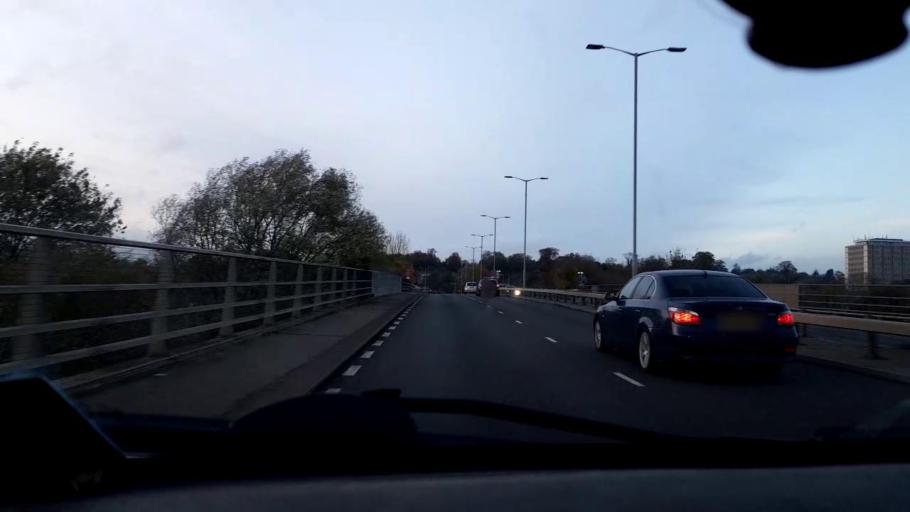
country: GB
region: England
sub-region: Norfolk
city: Thorpe Hamlet
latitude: 52.6104
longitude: 1.3093
